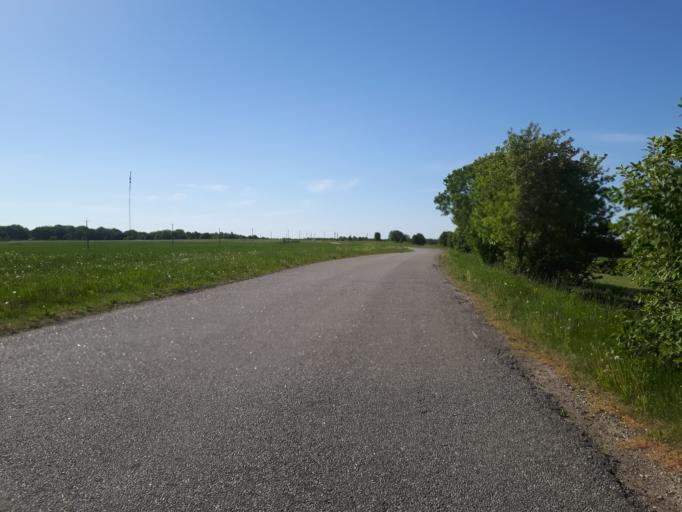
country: EE
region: Laeaene-Virumaa
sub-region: Haljala vald
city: Haljala
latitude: 59.5453
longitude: 26.1432
